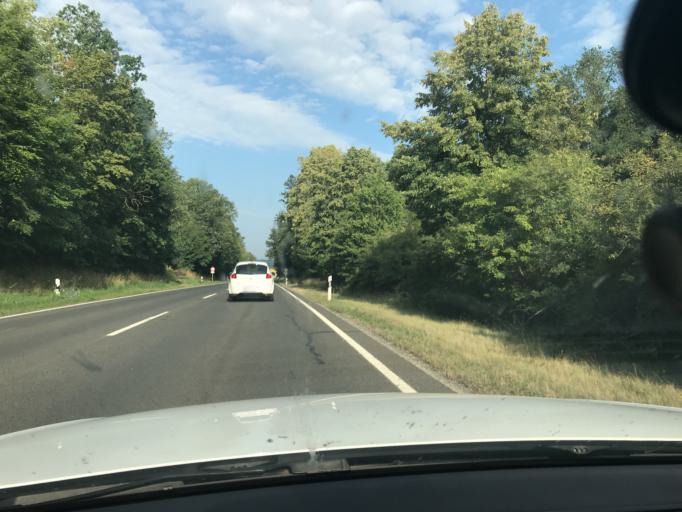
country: DE
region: Bavaria
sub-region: Upper Palatinate
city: Auerbach
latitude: 49.6988
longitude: 11.6141
